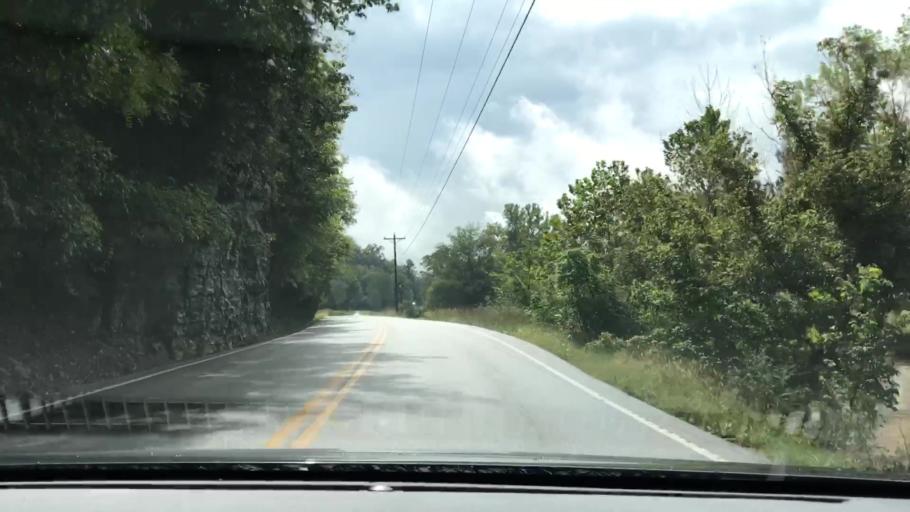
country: US
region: Tennessee
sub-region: Smith County
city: Carthage
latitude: 36.3304
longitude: -85.9650
